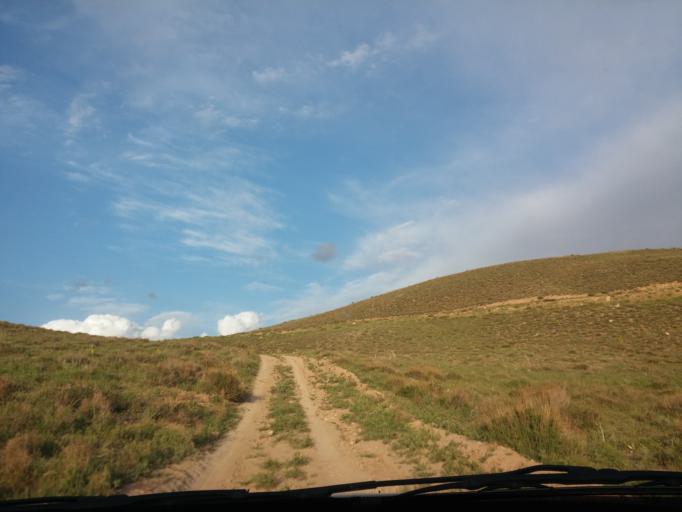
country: IR
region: Semnan
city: Istgah-e Rah Ahan-e Garmsar
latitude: 35.4903
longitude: 52.3043
